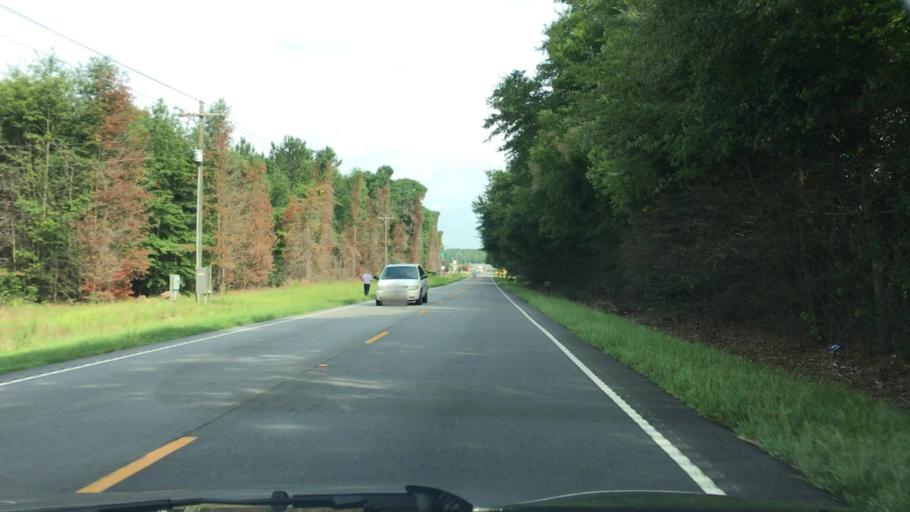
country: US
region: South Carolina
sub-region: Lexington County
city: Batesburg
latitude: 33.7463
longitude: -81.5216
